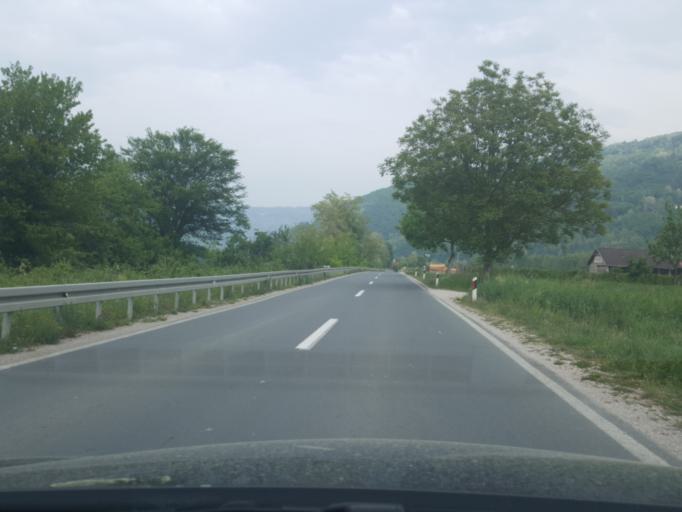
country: RS
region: Central Serbia
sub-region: Zlatiborski Okrug
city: Bajina Basta
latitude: 44.0012
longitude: 19.5777
